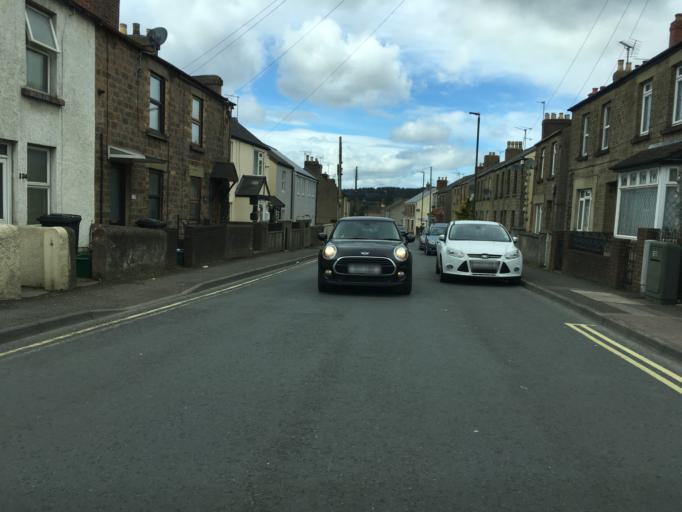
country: GB
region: England
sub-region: Gloucestershire
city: Cinderford
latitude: 51.8294
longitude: -2.5034
